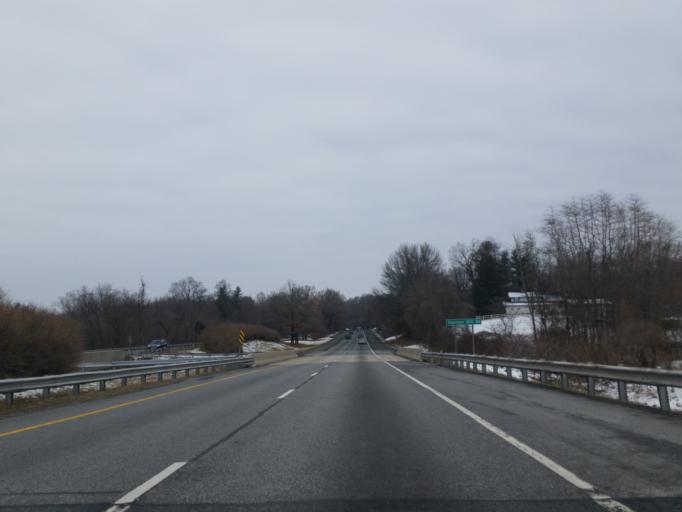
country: US
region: Maryland
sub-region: Baltimore County
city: Hunt Valley
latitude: 39.5208
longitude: -76.6611
